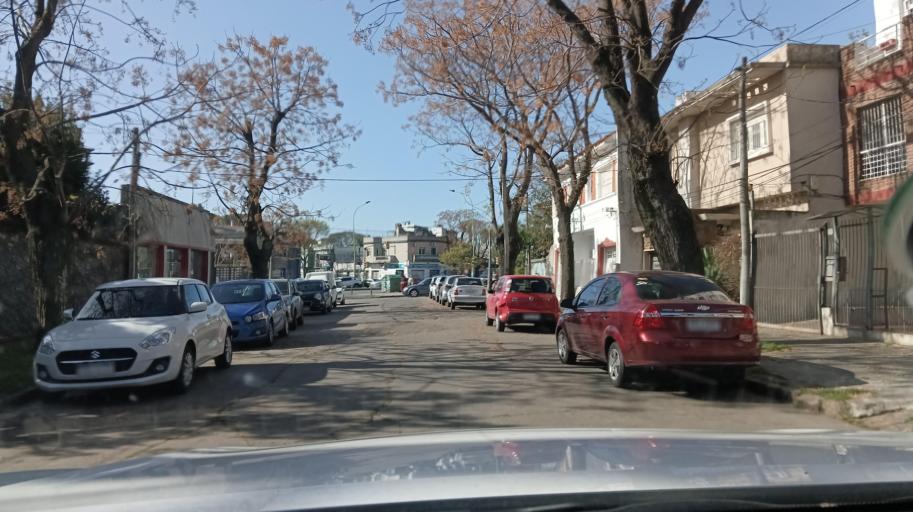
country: UY
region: Montevideo
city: Montevideo
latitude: -34.8724
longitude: -56.1946
